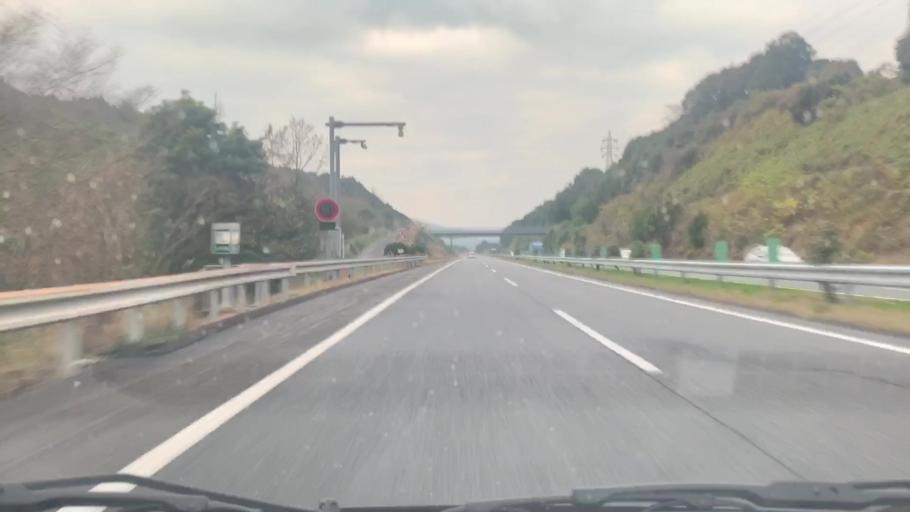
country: JP
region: Nagasaki
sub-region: Isahaya-shi
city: Isahaya
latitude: 32.8221
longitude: 129.9957
